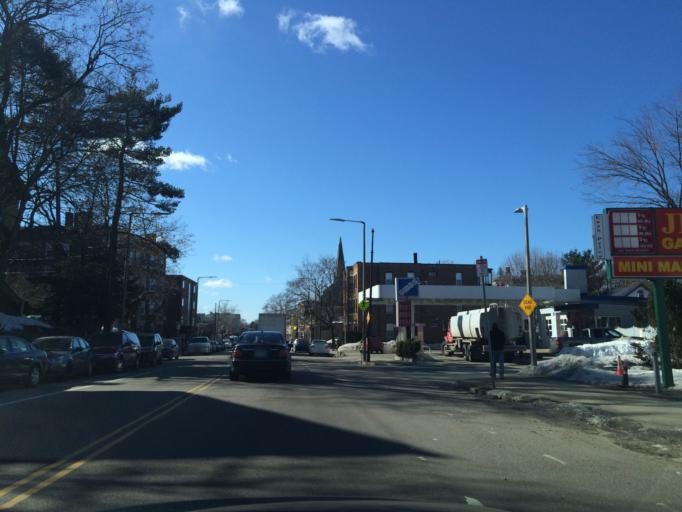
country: US
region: Massachusetts
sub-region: Suffolk County
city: Jamaica Plain
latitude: 42.3158
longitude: -71.1141
